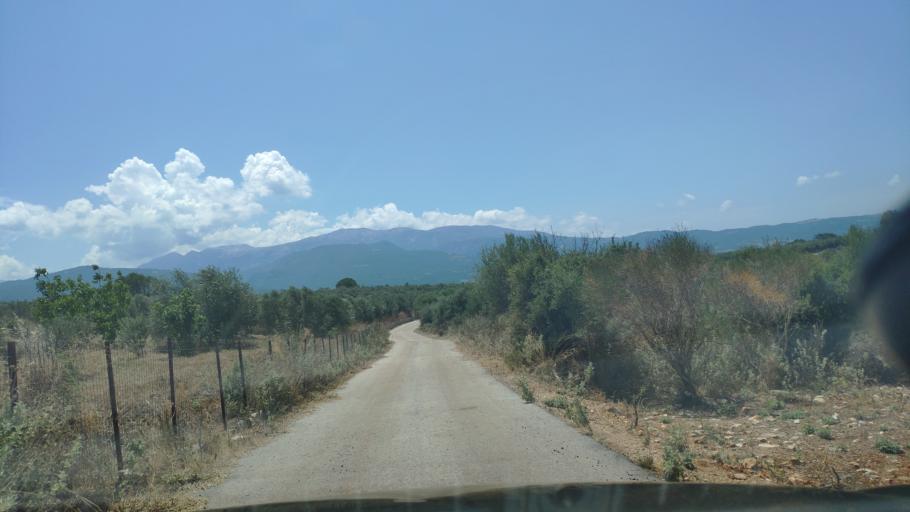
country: GR
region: West Greece
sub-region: Nomos Aitolias kai Akarnanias
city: Amfilochia
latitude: 38.9047
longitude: 21.0982
